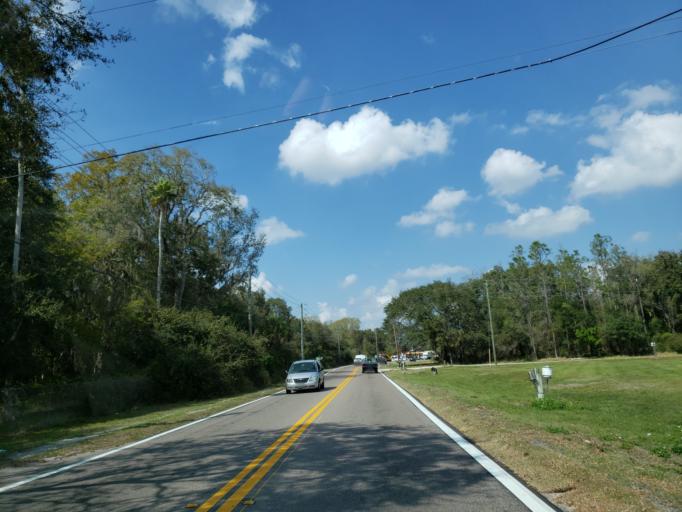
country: US
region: Florida
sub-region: Hillsborough County
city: Keystone
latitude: 28.1467
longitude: -82.5787
